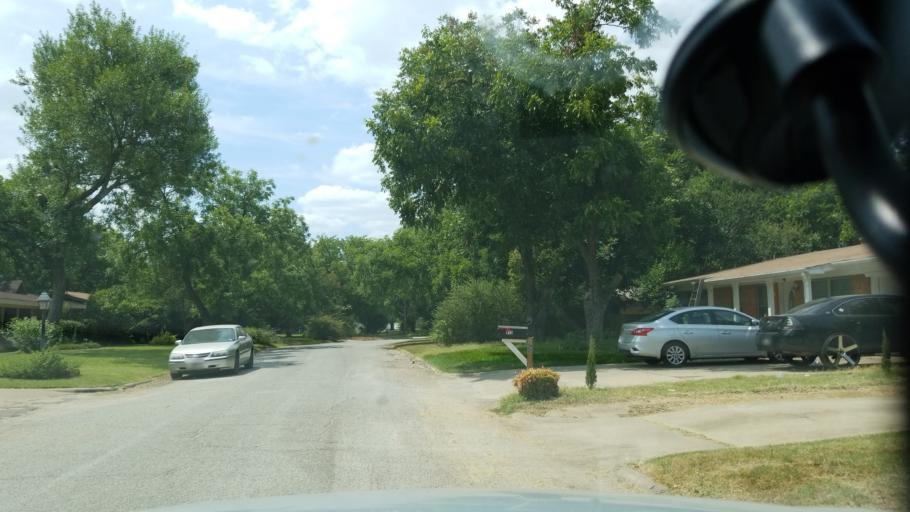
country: US
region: Texas
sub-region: Dallas County
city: Grand Prairie
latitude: 32.7558
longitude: -96.9870
